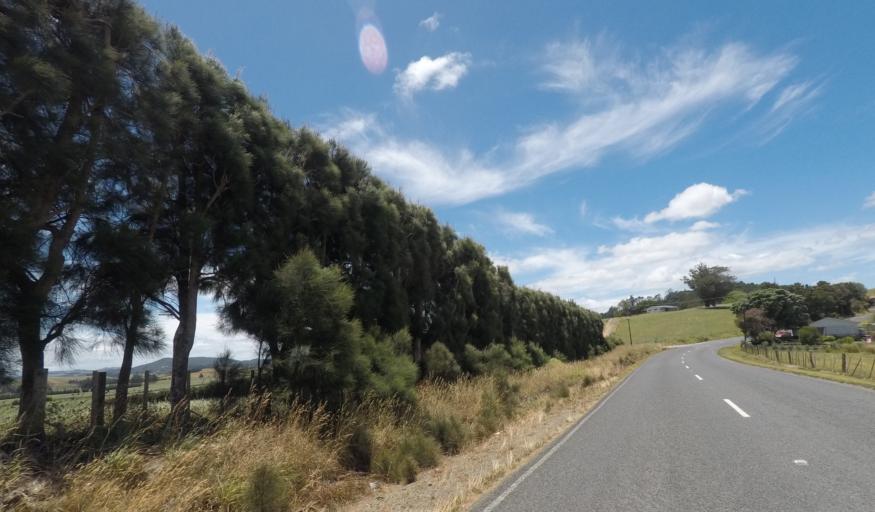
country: NZ
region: Northland
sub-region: Whangarei
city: Whangarei
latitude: -35.5599
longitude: 174.2872
